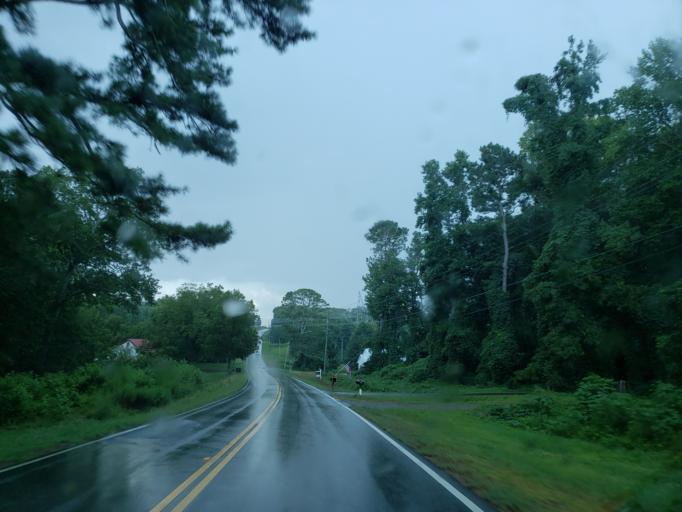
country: US
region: Georgia
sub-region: Cherokee County
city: Canton
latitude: 34.3209
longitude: -84.4677
